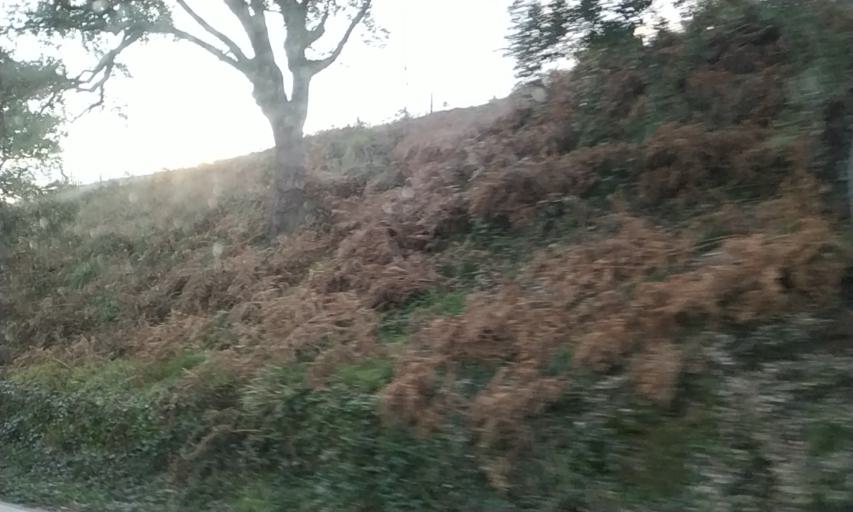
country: PT
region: Vila Real
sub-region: Mondim de Basto
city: Mondim de Basto
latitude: 41.4623
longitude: -7.9562
